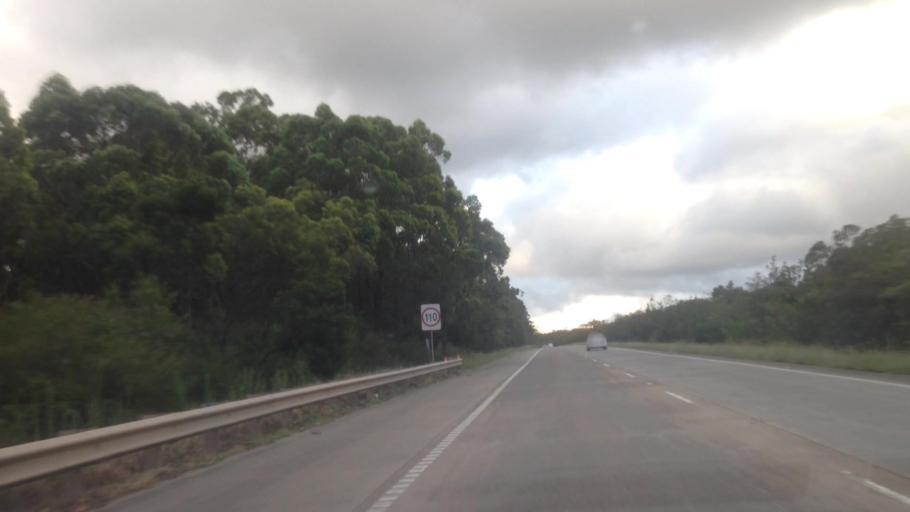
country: AU
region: New South Wales
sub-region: Wyong Shire
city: Jilliby
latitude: -33.2053
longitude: 151.4574
